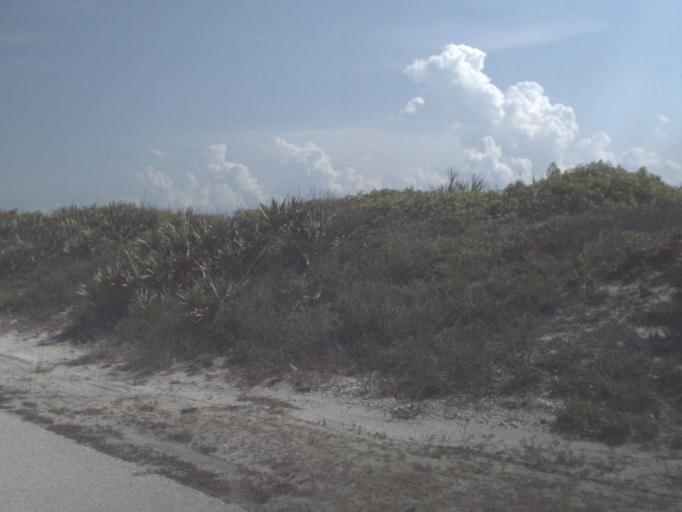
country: US
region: Florida
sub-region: Saint Johns County
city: Villano Beach
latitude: 30.0034
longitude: -81.3185
